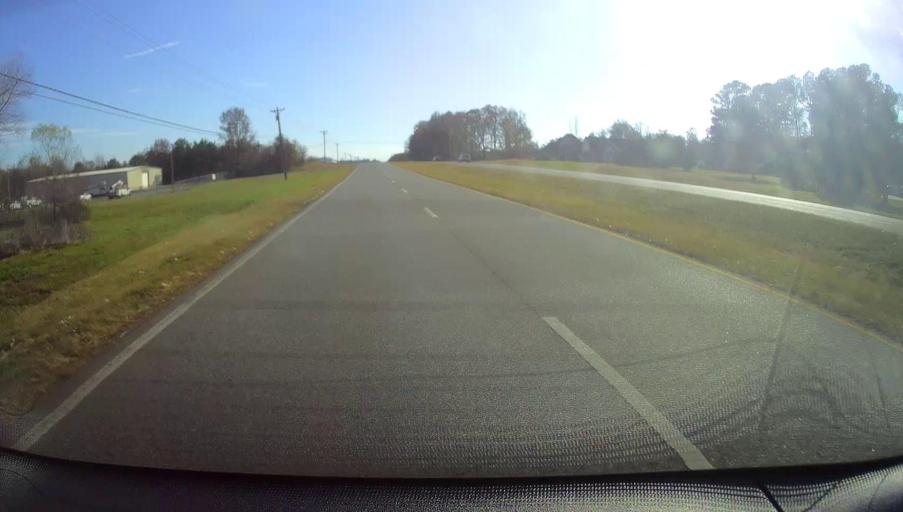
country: US
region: Alabama
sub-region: Limestone County
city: Athens
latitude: 34.7233
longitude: -86.9569
